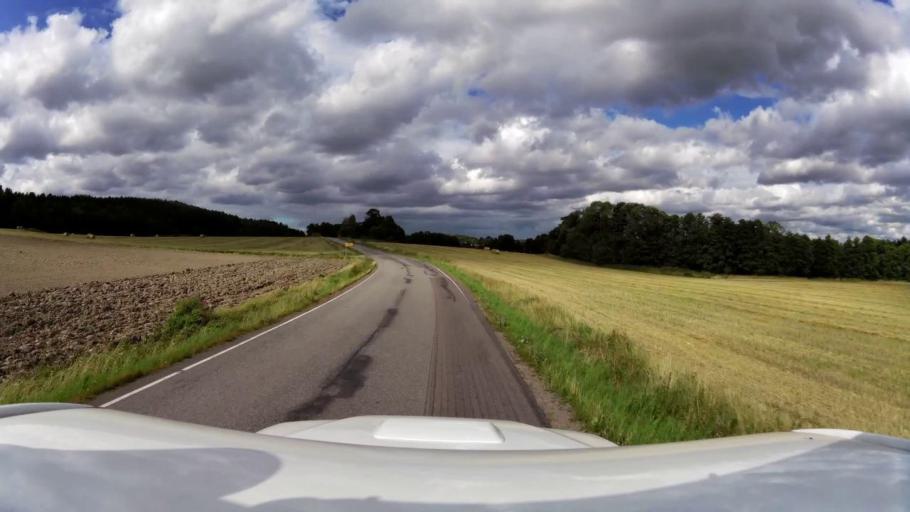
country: SE
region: OEstergoetland
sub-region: Linkopings Kommun
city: Sturefors
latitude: 58.3161
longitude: 15.7222
